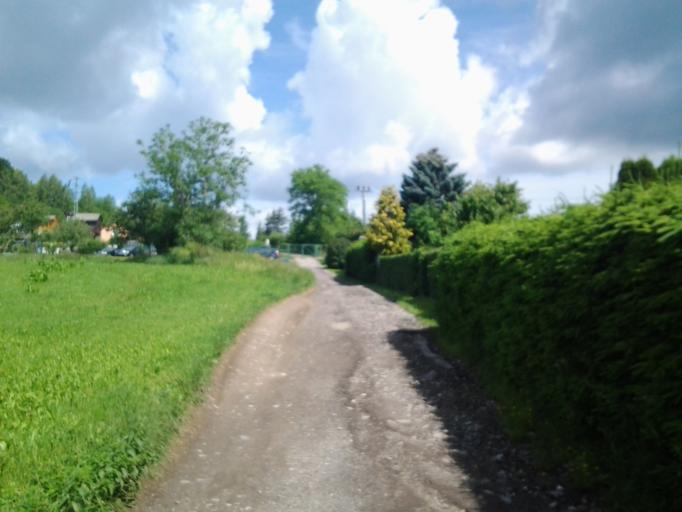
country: CZ
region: Jihocesky
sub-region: Okres Cesky Krumlov
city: Cesky Krumlov
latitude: 48.8212
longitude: 14.3095
